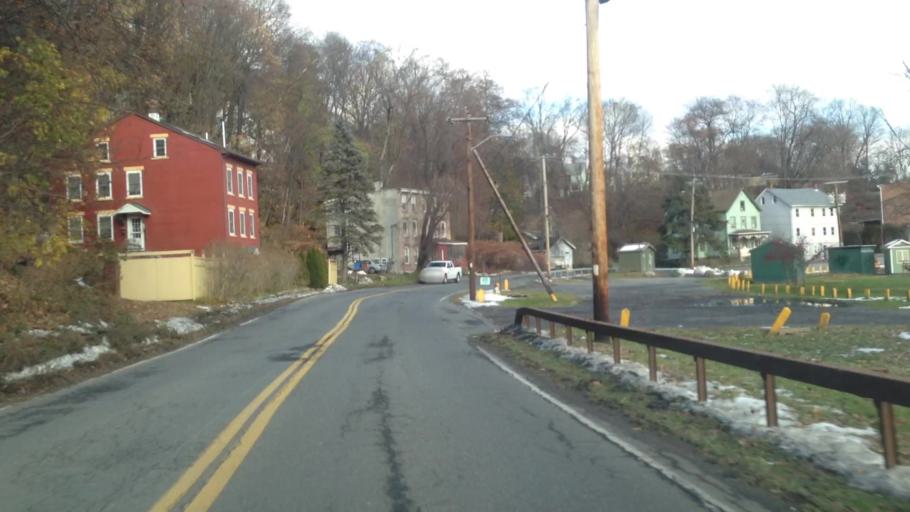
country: US
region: New York
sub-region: Ulster County
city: Kingston
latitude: 41.9147
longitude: -73.9933
